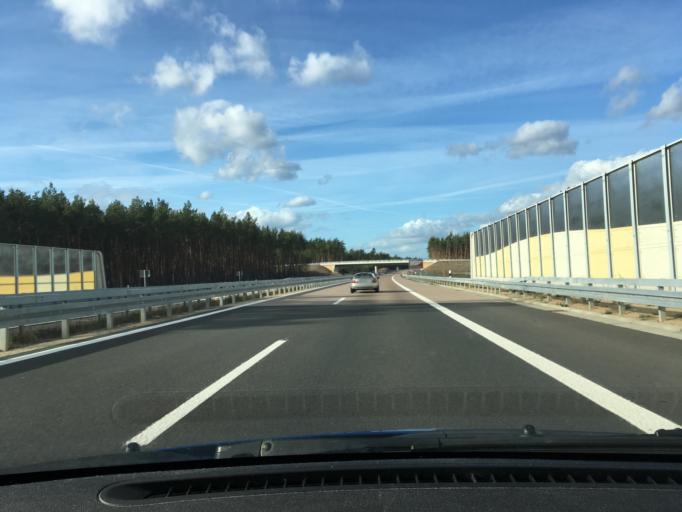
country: DE
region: Mecklenburg-Vorpommern
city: Grabow
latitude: 53.2607
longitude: 11.5356
